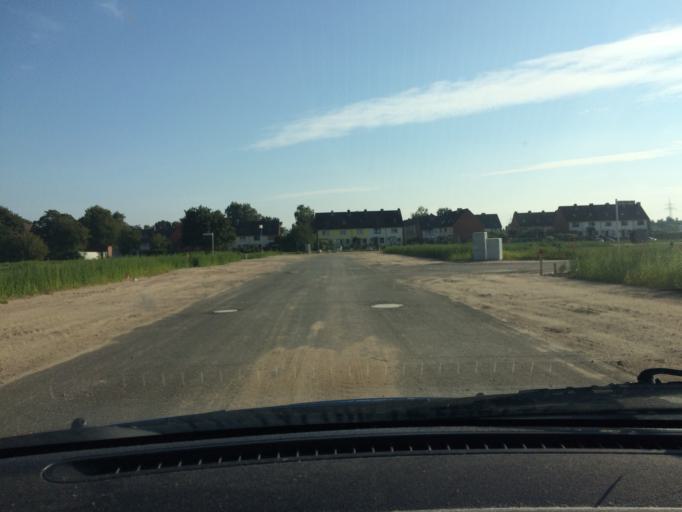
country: DE
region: Lower Saxony
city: Winsen
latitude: 53.3692
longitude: 10.1880
